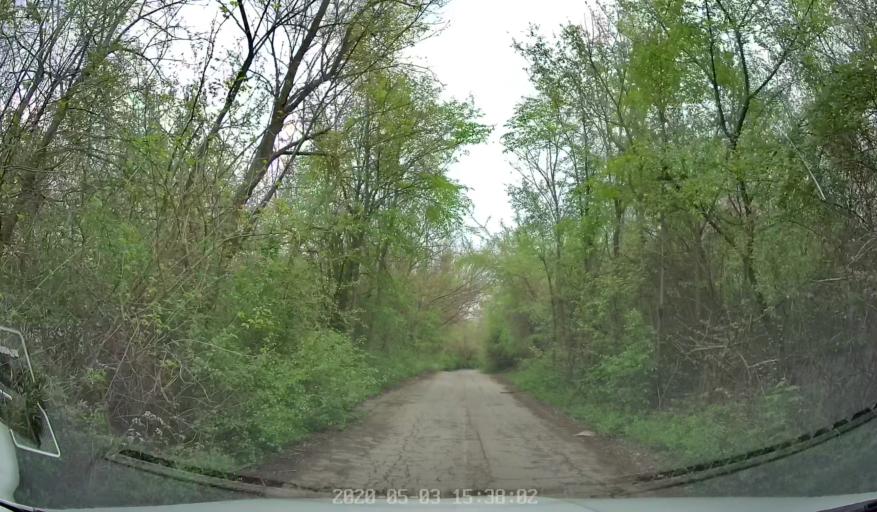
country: MD
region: Chisinau
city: Vatra
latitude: 47.0985
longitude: 28.7068
